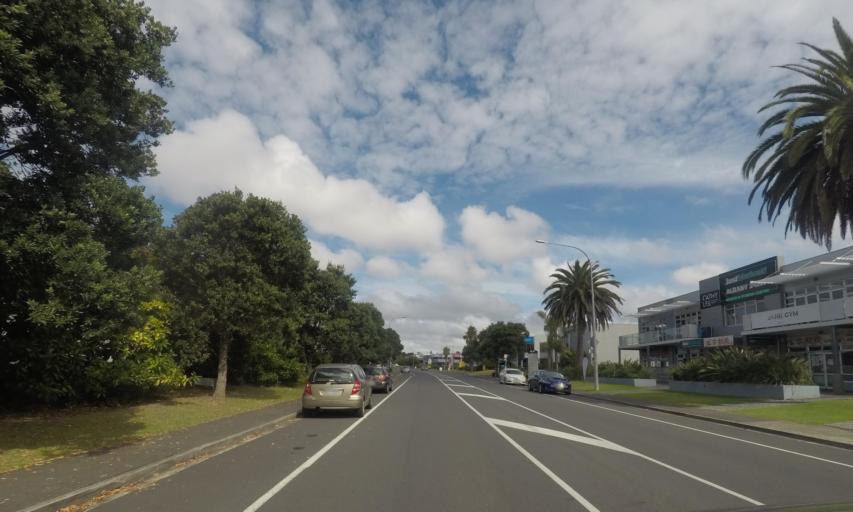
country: NZ
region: Auckland
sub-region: Auckland
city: Rothesay Bay
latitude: -36.7435
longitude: 174.6971
